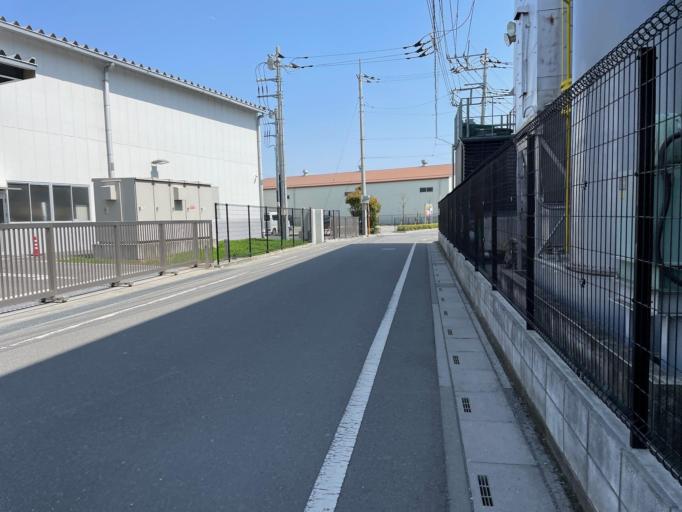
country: JP
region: Saitama
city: Sayama
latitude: 35.8736
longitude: 139.3960
